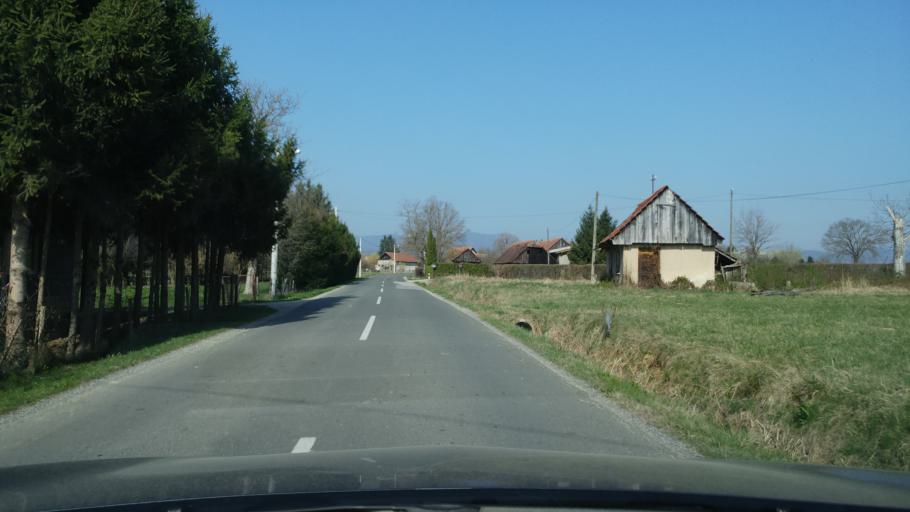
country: HR
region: Zagrebacka
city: Pojatno
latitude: 45.9775
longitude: 15.7342
